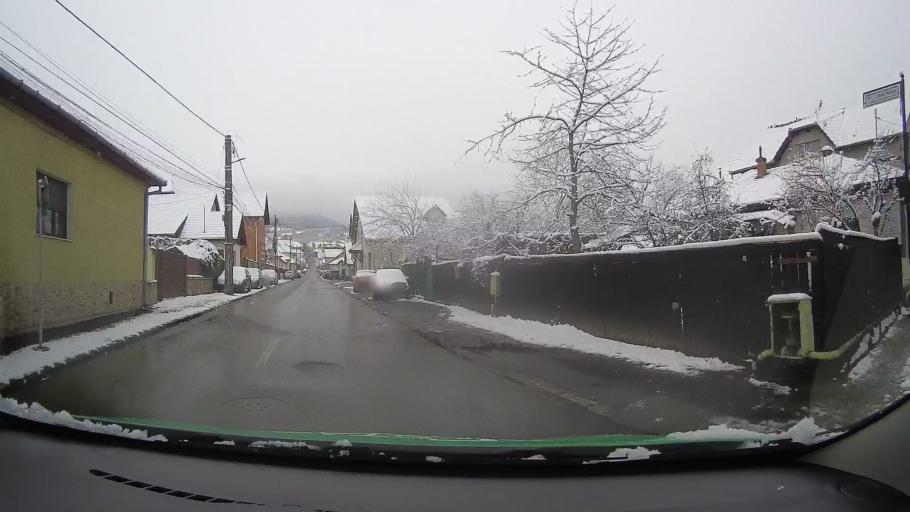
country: RO
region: Hunedoara
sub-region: Municipiul Deva
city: Deva
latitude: 45.8721
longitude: 22.9021
